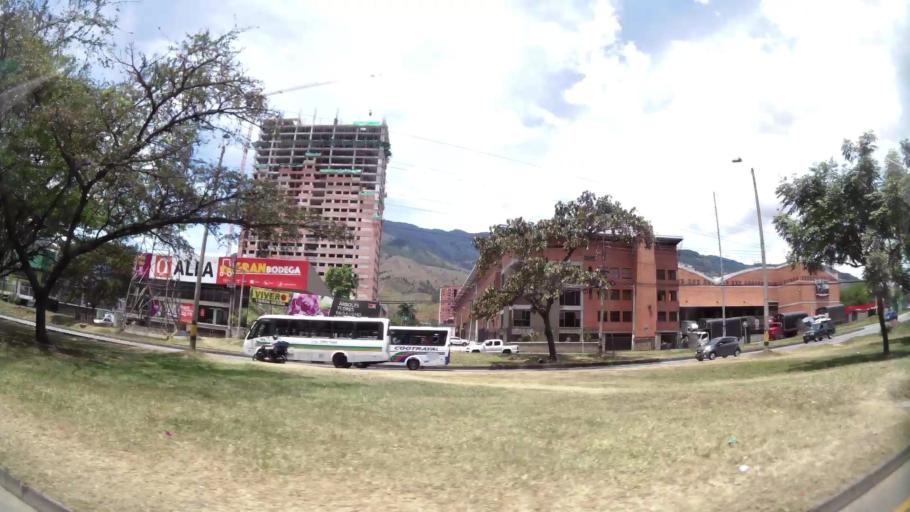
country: CO
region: Antioquia
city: Bello
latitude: 6.3388
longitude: -75.5404
